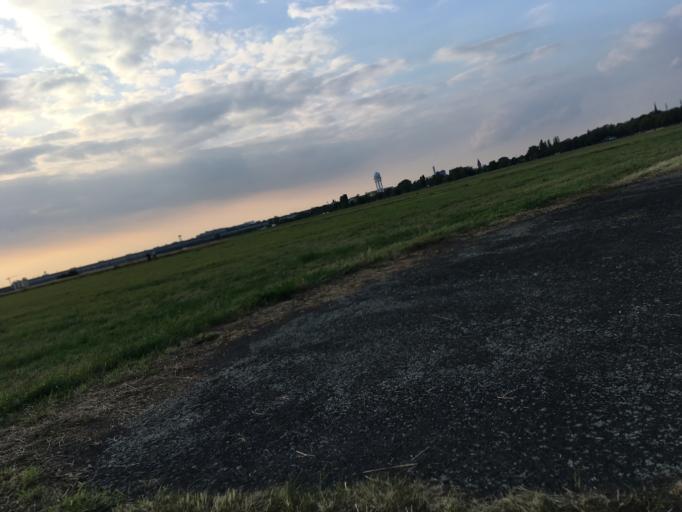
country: DE
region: Berlin
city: Tempelhof Bezirk
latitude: 52.4722
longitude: 13.4132
